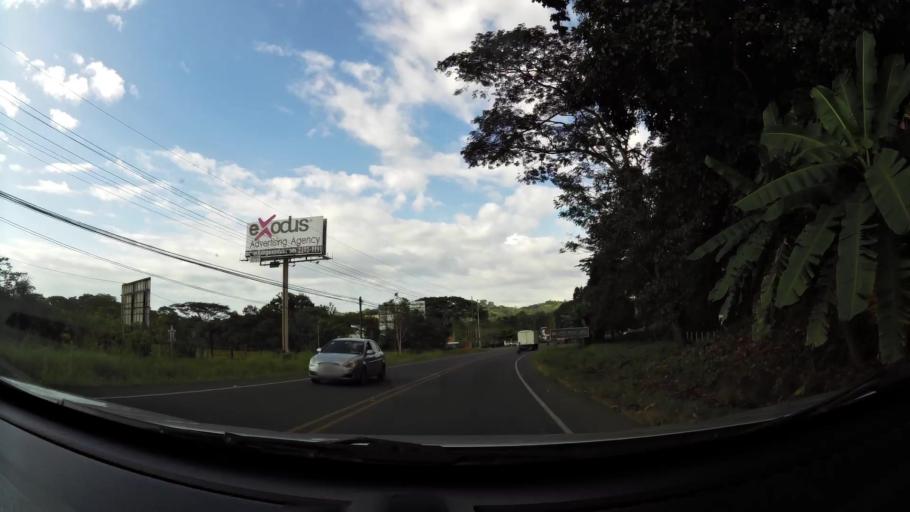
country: CR
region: Puntarenas
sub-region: Canton de Garabito
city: Jaco
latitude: 9.7106
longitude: -84.6362
